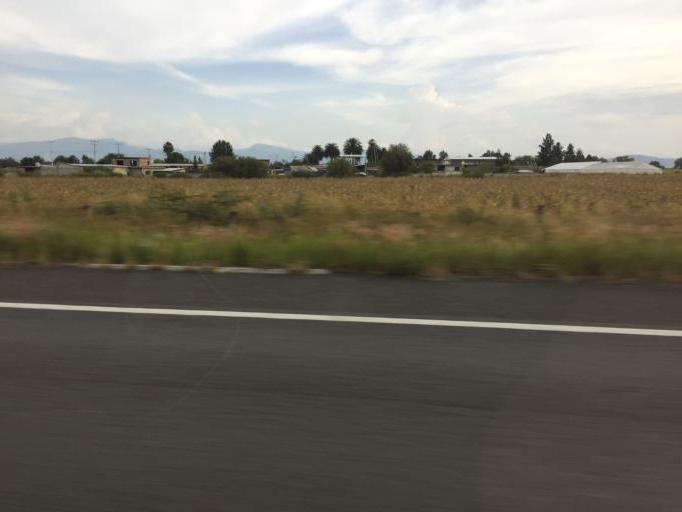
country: MX
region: Michoacan
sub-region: Alvaro Obregon
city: Lazaro Cardenas (La Purisima)
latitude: 19.8915
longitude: -101.0025
